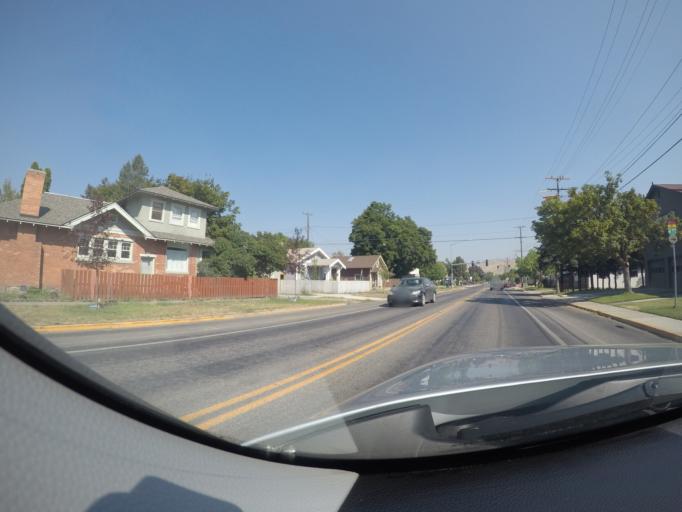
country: US
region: Montana
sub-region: Missoula County
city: Missoula
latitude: 46.8632
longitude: -113.9892
